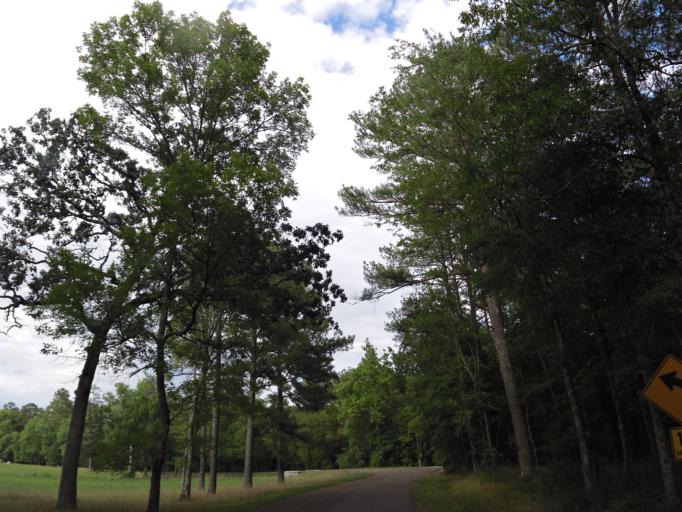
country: US
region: Georgia
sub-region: Walker County
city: Fairview
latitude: 34.9124
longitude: -85.2672
